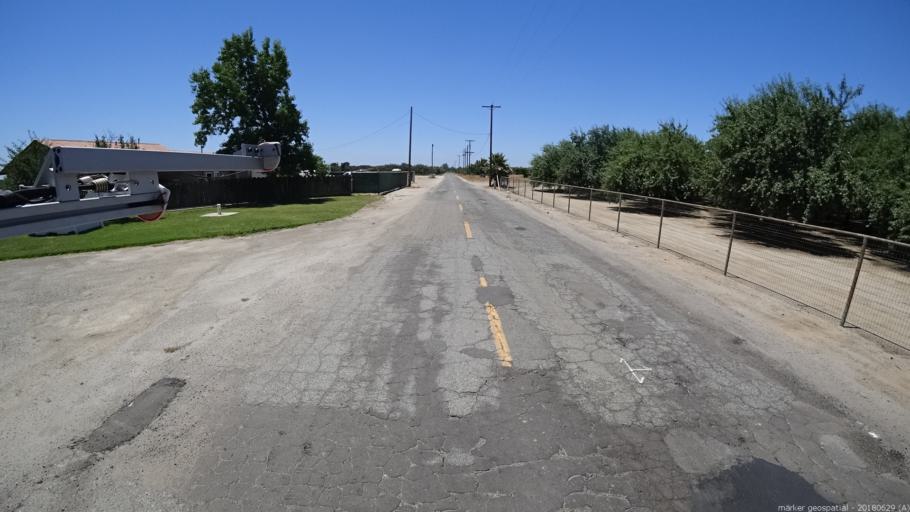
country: US
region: California
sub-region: Madera County
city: Parksdale
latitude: 37.0019
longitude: -119.9990
